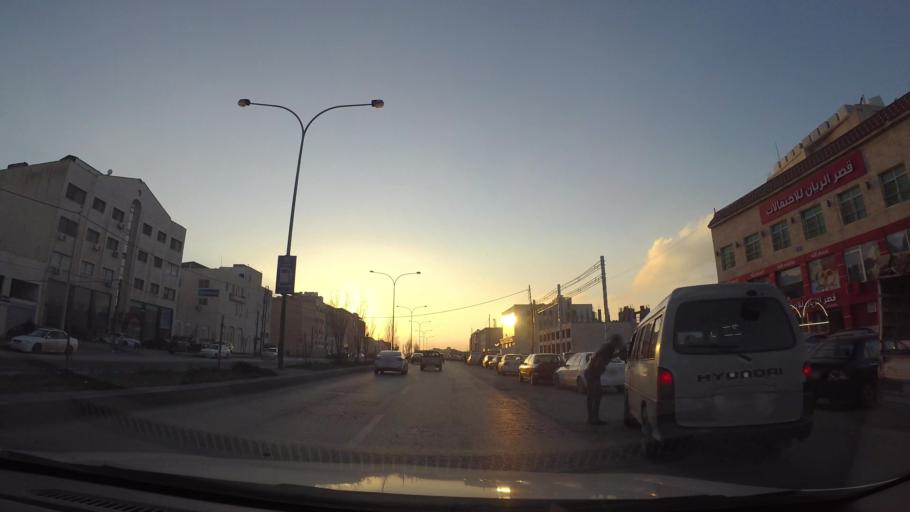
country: JO
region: Amman
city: Al Quwaysimah
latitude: 31.9004
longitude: 35.9307
